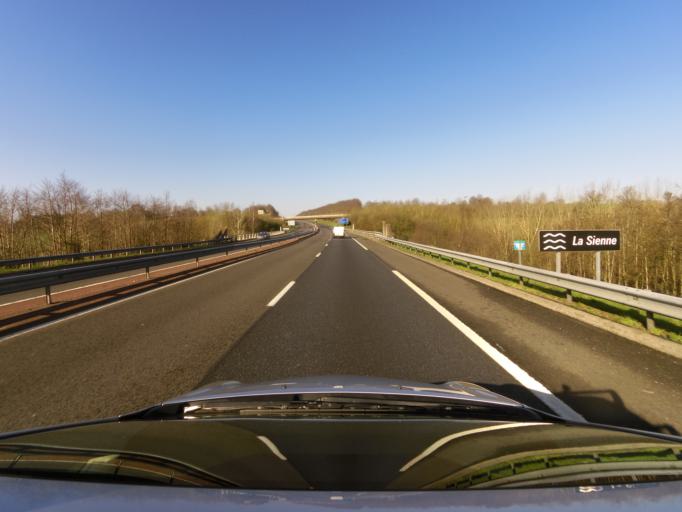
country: FR
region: Lower Normandy
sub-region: Departement de la Manche
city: Villedieu-les-Poeles
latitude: 48.8574
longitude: -1.2190
